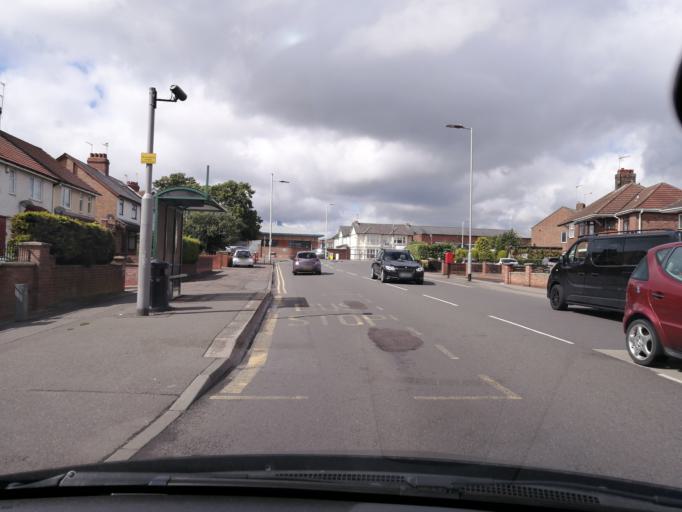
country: GB
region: England
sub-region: Peterborough
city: Peterborough
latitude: 52.5584
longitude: -0.2494
